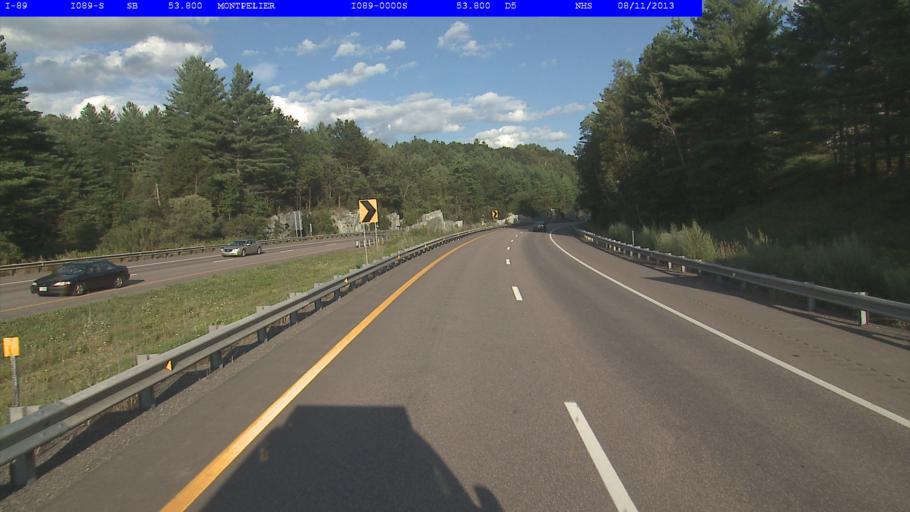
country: US
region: Vermont
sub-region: Washington County
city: Montpelier
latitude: 44.2608
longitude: -72.6058
